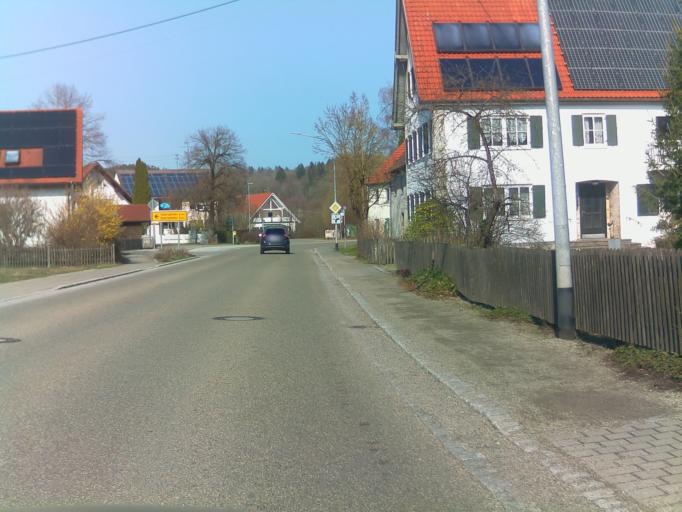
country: DE
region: Bavaria
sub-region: Swabia
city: Ebershausen
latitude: 48.2042
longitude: 10.3130
